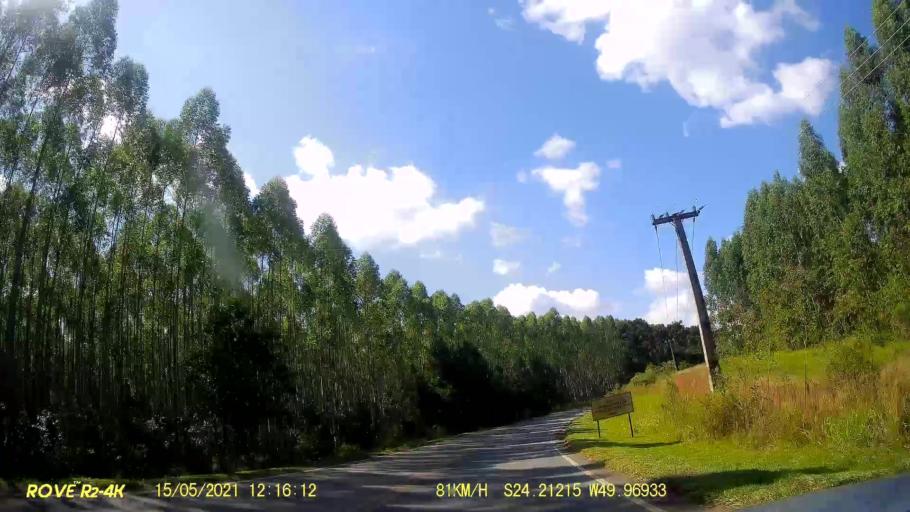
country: BR
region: Parana
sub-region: Jaguariaiva
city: Jaguariaiva
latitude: -24.2123
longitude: -49.9694
